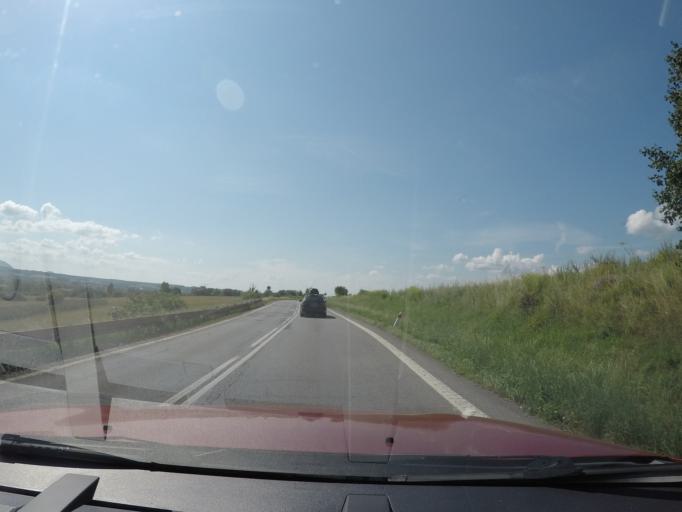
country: SK
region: Presovsky
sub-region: Okres Presov
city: Presov
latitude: 48.9389
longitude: 21.2398
